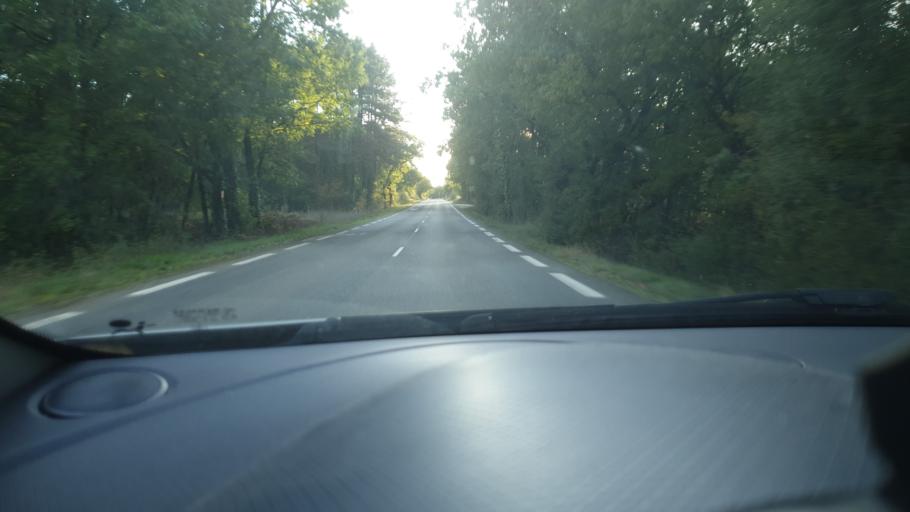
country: FR
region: Midi-Pyrenees
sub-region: Departement du Lot
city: Montcuq
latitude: 44.4040
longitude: 1.2442
